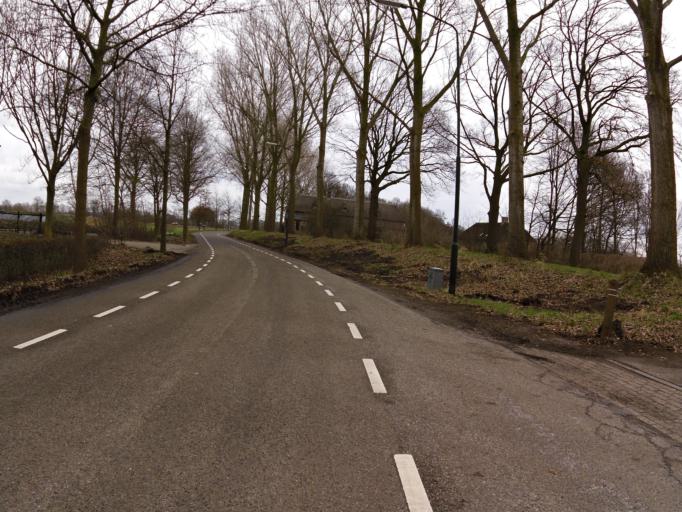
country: NL
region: North Brabant
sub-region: Gemeente Sint-Michielsgestel
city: Sint-Michielsgestel
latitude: 51.6594
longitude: 5.3408
